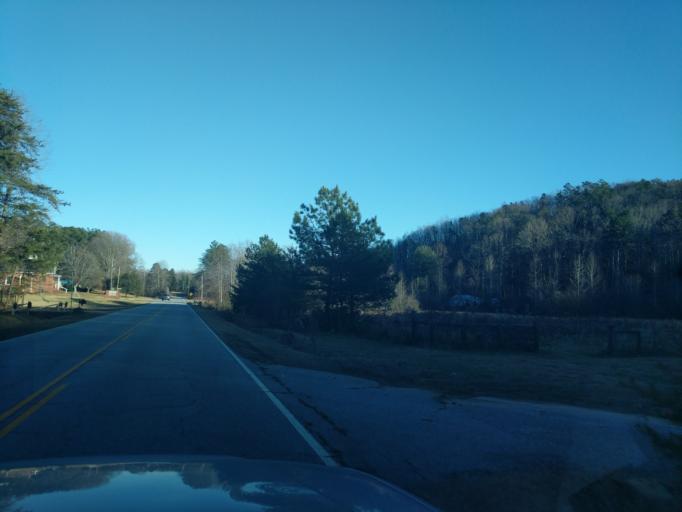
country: US
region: South Carolina
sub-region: Oconee County
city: Westminster
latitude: 34.7231
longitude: -83.2198
